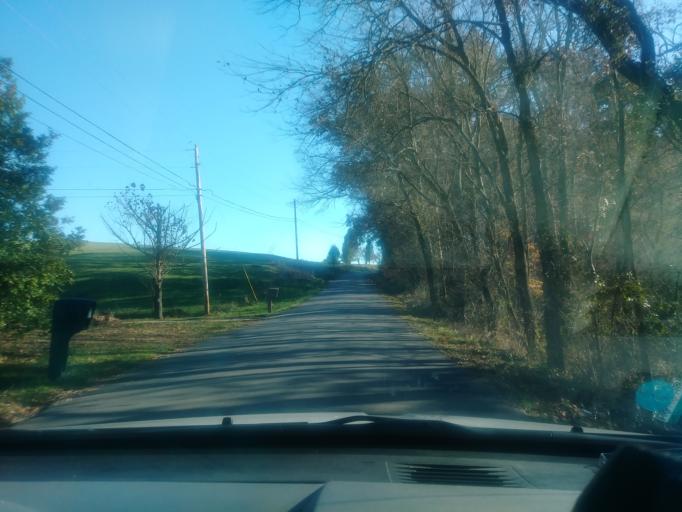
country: US
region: Tennessee
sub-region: Greene County
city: Greeneville
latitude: 36.0765
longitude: -82.8860
